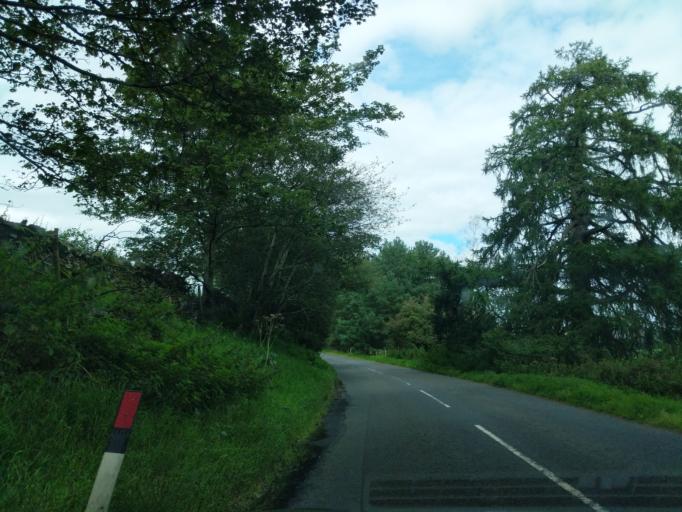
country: GB
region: Scotland
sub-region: The Scottish Borders
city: Peebles
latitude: 55.6370
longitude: -3.2835
